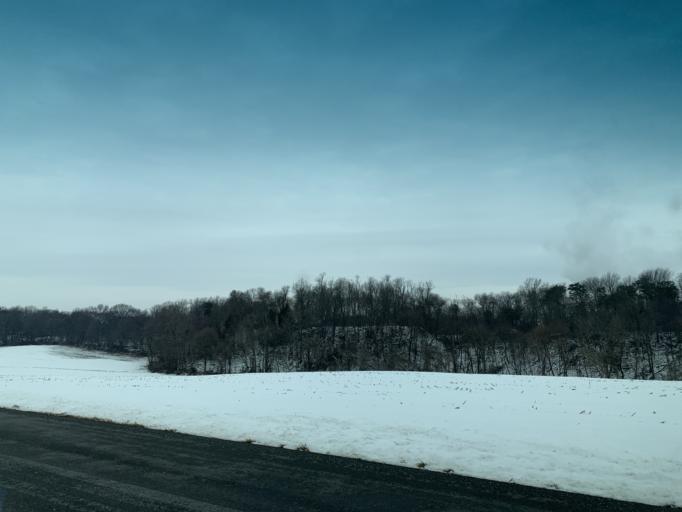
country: US
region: Pennsylvania
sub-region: York County
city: Susquehanna Trails
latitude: 39.7298
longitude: -76.3037
